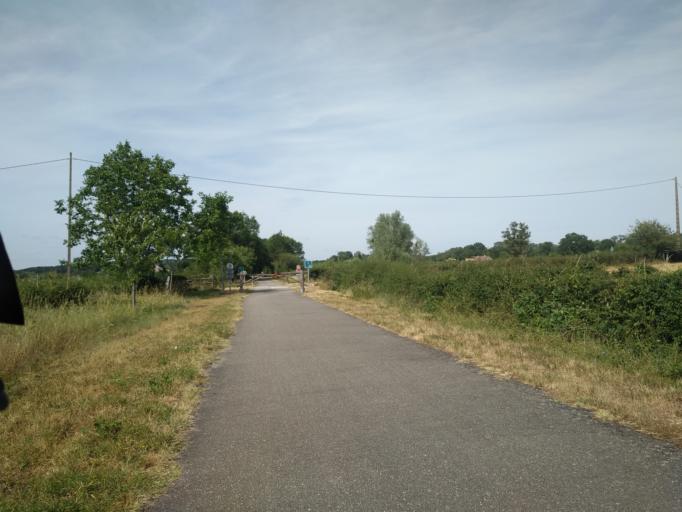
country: FR
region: Auvergne
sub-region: Departement de l'Allier
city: Diou
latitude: 46.5609
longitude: 3.7472
